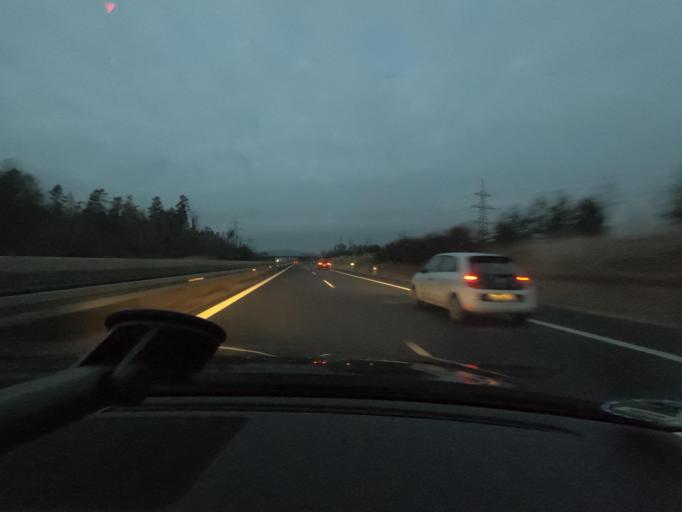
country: DE
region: Bavaria
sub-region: Upper Franconia
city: Rodental
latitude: 50.2692
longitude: 11.0175
